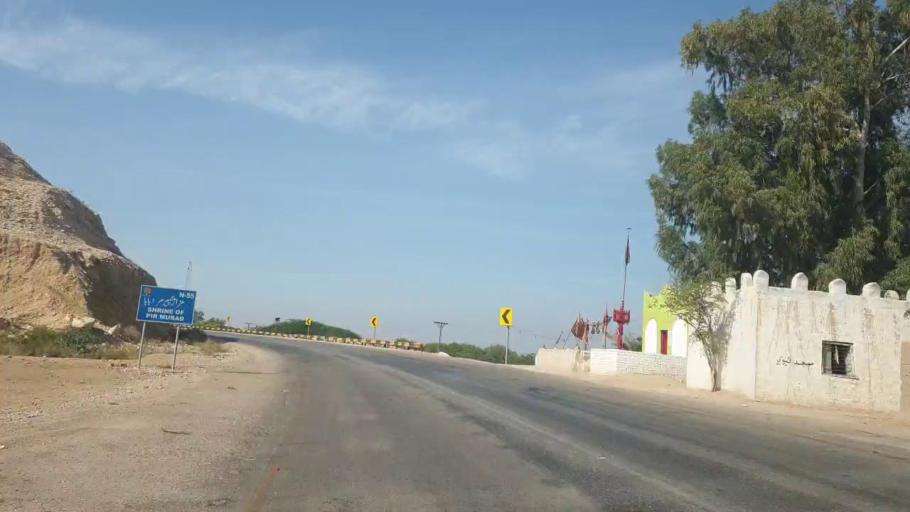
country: PK
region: Sindh
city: Sehwan
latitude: 26.3205
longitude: 67.8878
